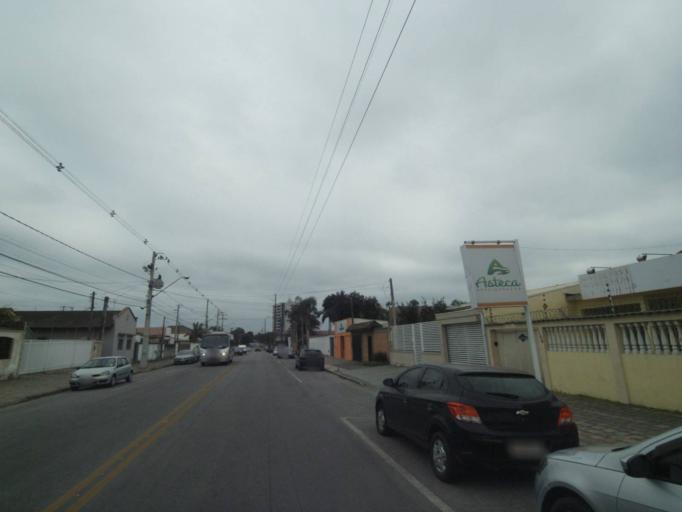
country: BR
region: Parana
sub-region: Paranagua
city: Paranagua
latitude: -25.5164
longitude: -48.5175
